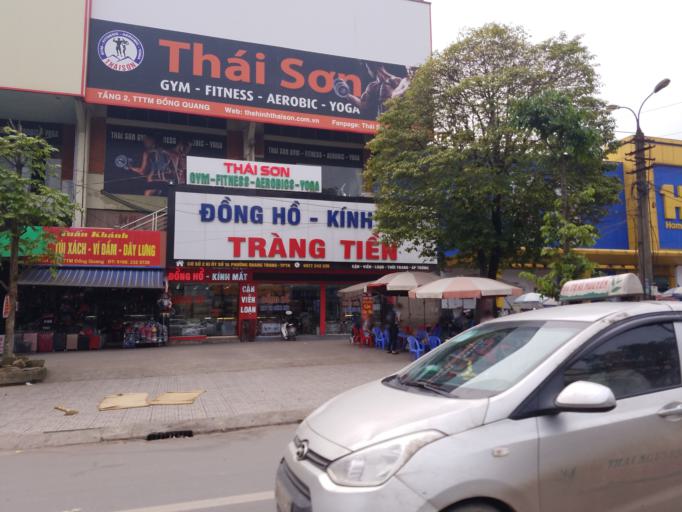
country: VN
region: Thai Nguyen
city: Thanh Pho Thai Nguyen
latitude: 21.5900
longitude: 105.8269
